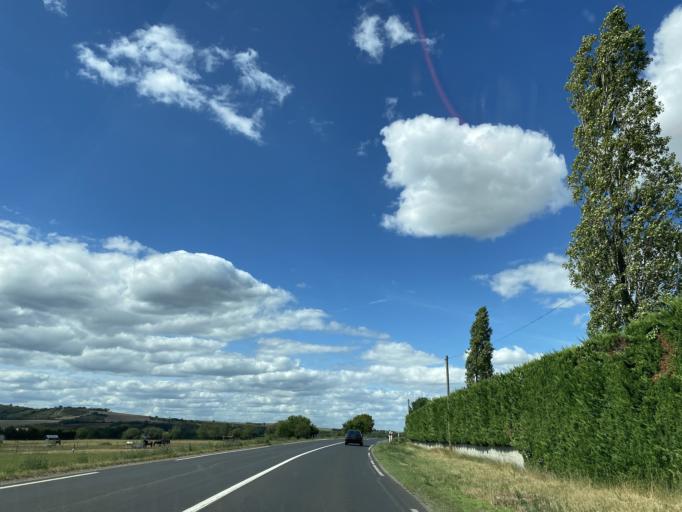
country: FR
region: Auvergne
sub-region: Departement du Puy-de-Dome
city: Mezel
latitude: 45.7511
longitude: 3.2380
